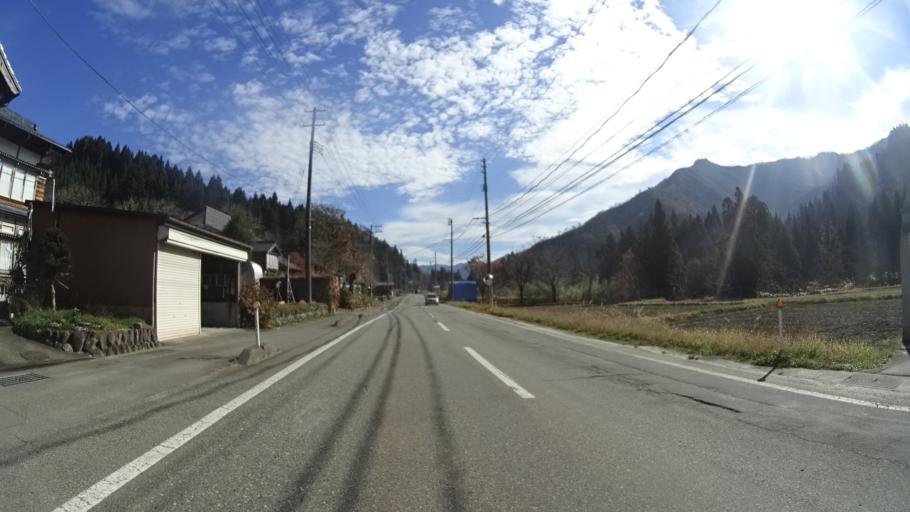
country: JP
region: Niigata
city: Muikamachi
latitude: 37.2245
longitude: 139.0217
